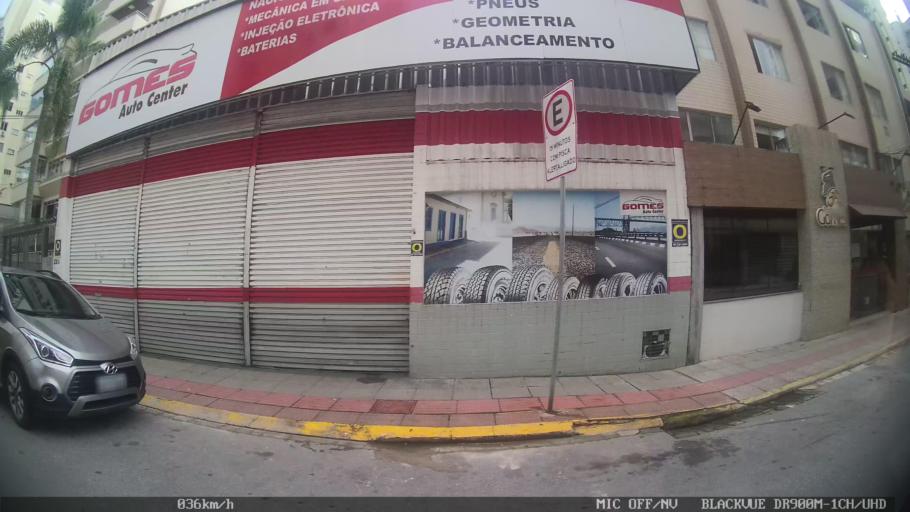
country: BR
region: Santa Catarina
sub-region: Florianopolis
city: Florianopolis
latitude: -27.5900
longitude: -48.5576
